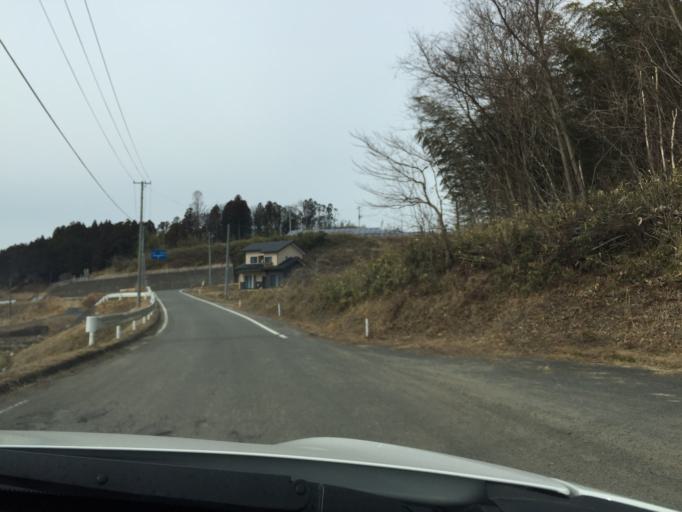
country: JP
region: Fukushima
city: Ishikawa
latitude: 37.2037
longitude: 140.5647
